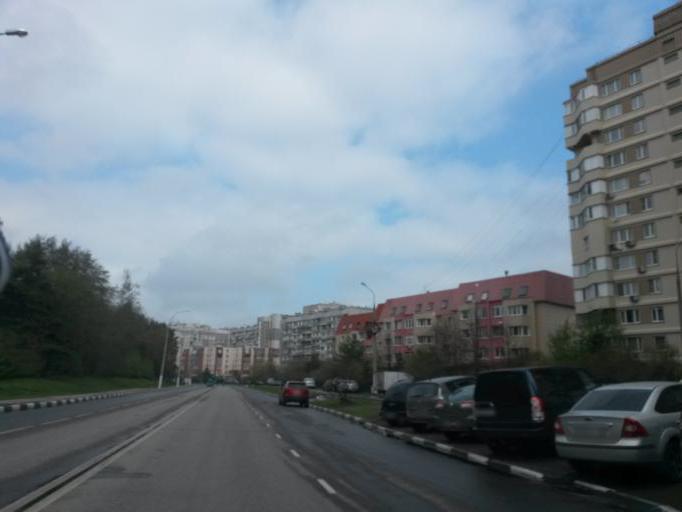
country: RU
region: Moscow
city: Annino
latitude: 55.5633
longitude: 37.5689
